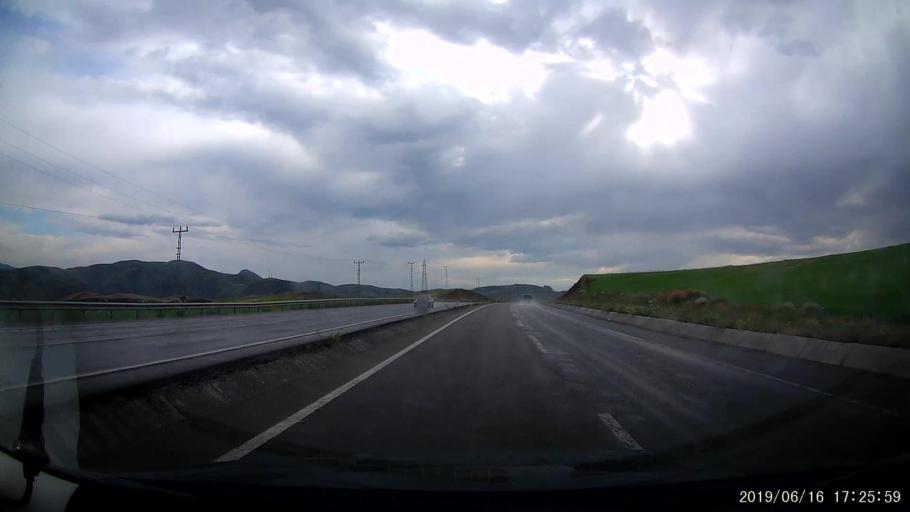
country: TR
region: Erzincan
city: Tercan
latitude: 39.7663
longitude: 40.4229
